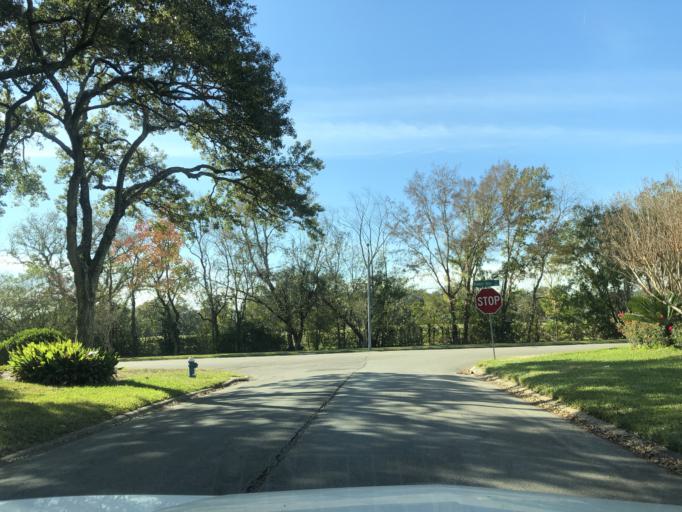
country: US
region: Texas
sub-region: Harris County
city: Bellaire
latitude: 29.6801
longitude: -95.5178
